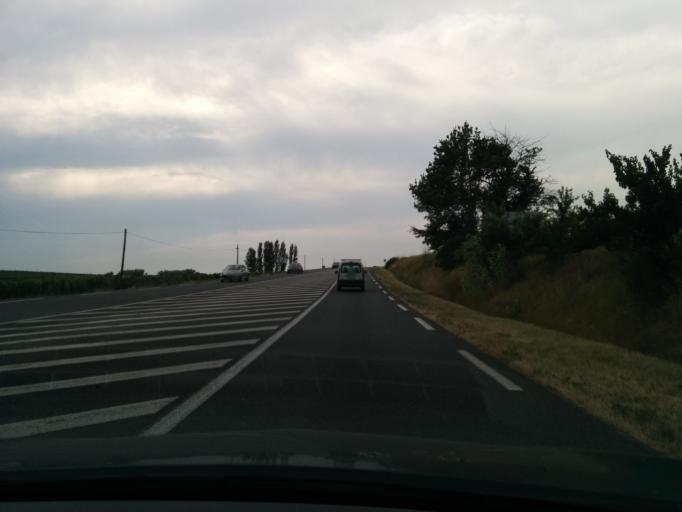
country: FR
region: Languedoc-Roussillon
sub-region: Departement de l'Aude
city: Pezens
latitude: 43.2479
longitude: 2.2877
